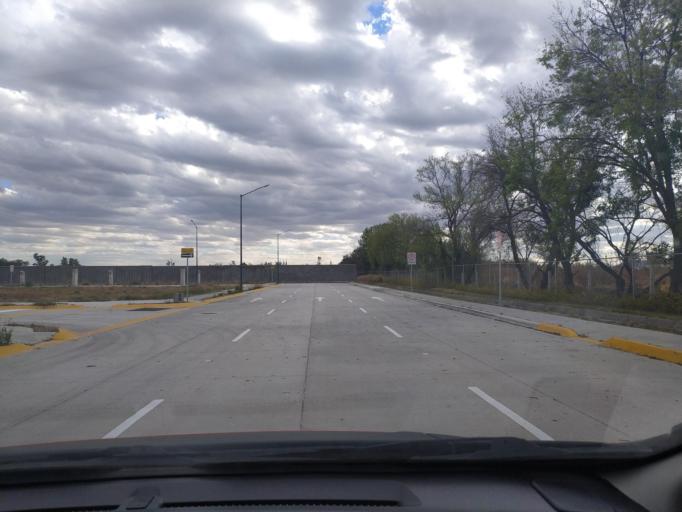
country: LA
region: Oudomxai
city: Muang La
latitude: 21.0236
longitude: 101.8244
